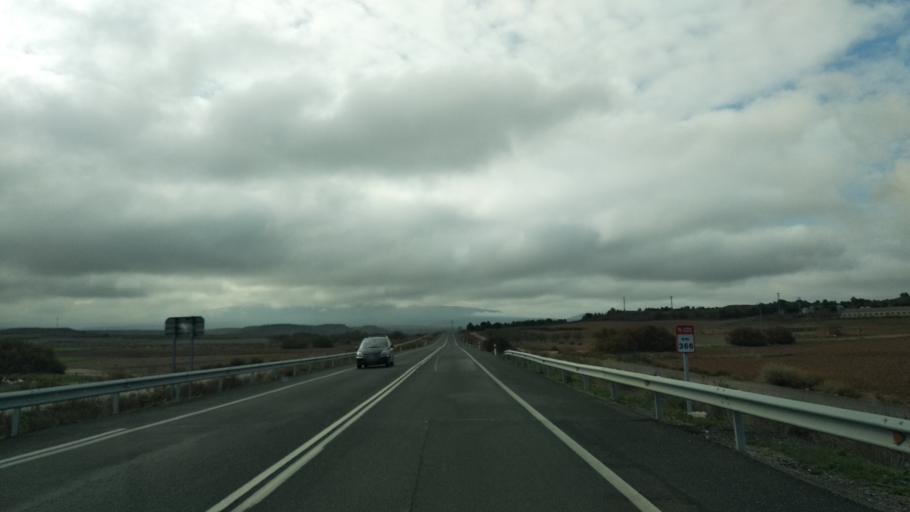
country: ES
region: La Rioja
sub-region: Provincia de La Rioja
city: Pradejon
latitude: 42.3209
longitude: -2.0267
